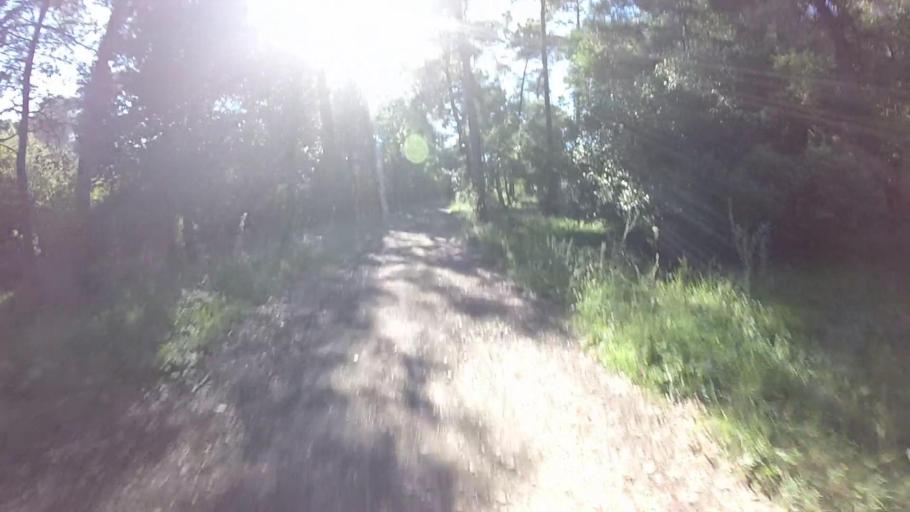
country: FR
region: Provence-Alpes-Cote d'Azur
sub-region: Departement des Alpes-Maritimes
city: Mougins
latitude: 43.6087
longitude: 7.0247
